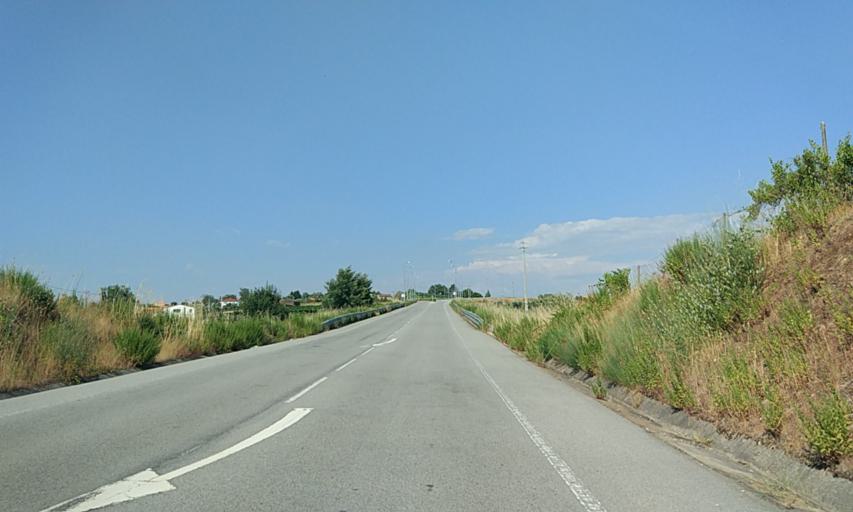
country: PT
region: Vila Real
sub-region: Sabrosa
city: Sabrosa
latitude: 41.2596
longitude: -7.4969
